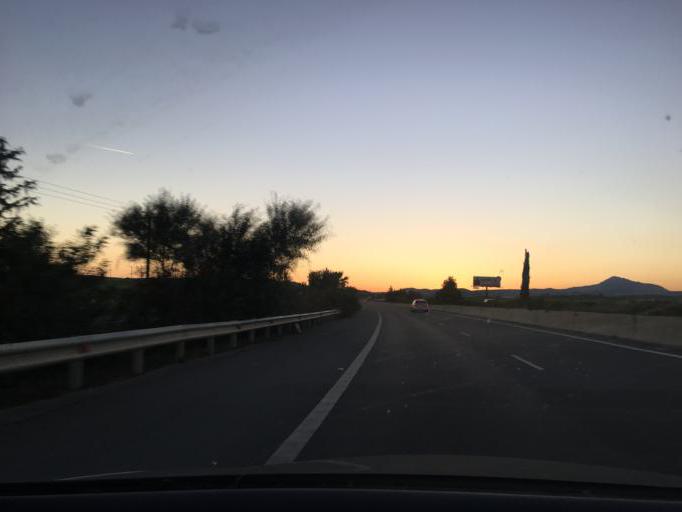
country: CY
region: Larnaka
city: Dhromolaxia
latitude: 34.9061
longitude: 33.5577
